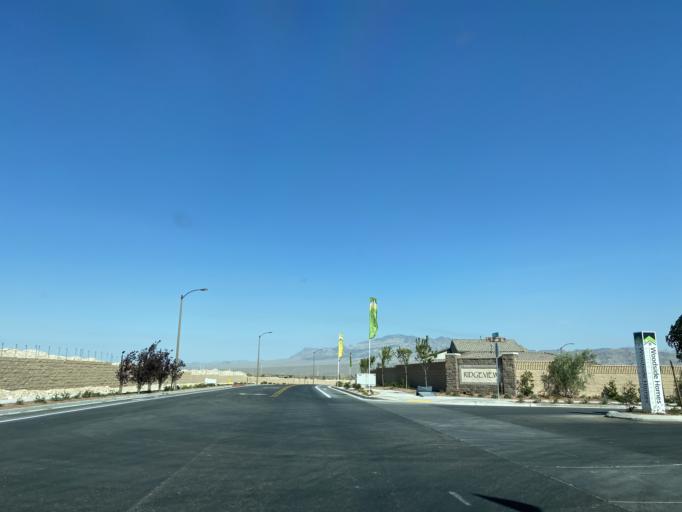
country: US
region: Nevada
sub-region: Clark County
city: Summerlin South
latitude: 36.3183
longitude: -115.3126
